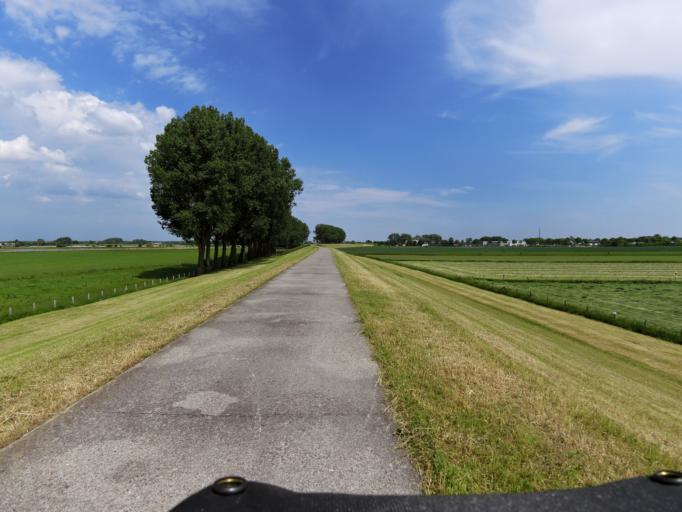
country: NL
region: North Brabant
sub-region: Gemeente Woudrichem
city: Woudrichem
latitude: 51.8165
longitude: 5.0717
